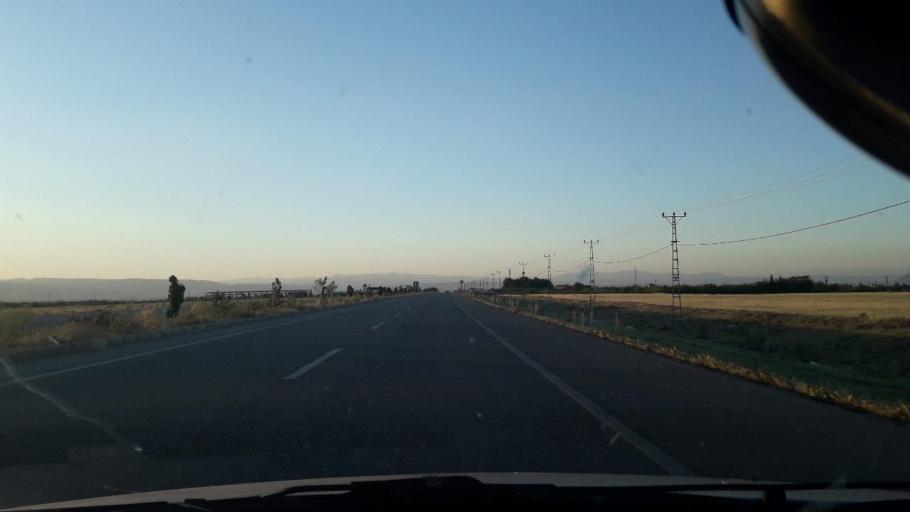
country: TR
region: Malatya
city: Yesilyurt
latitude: 38.3788
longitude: 38.2252
